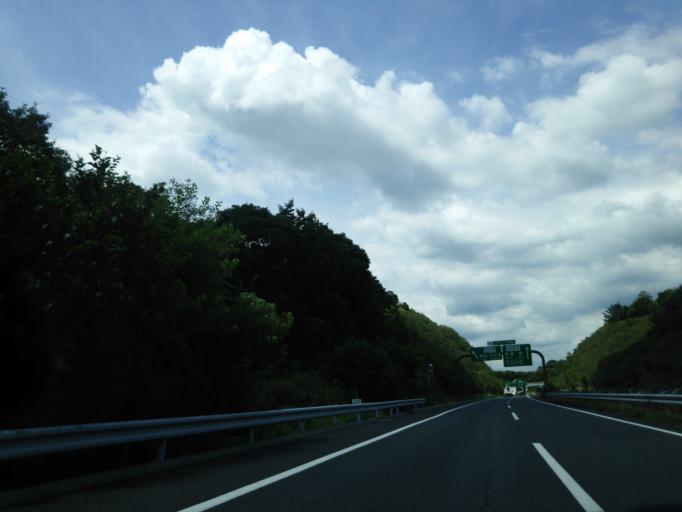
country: JP
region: Gifu
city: Toki
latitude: 35.3525
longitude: 137.1633
